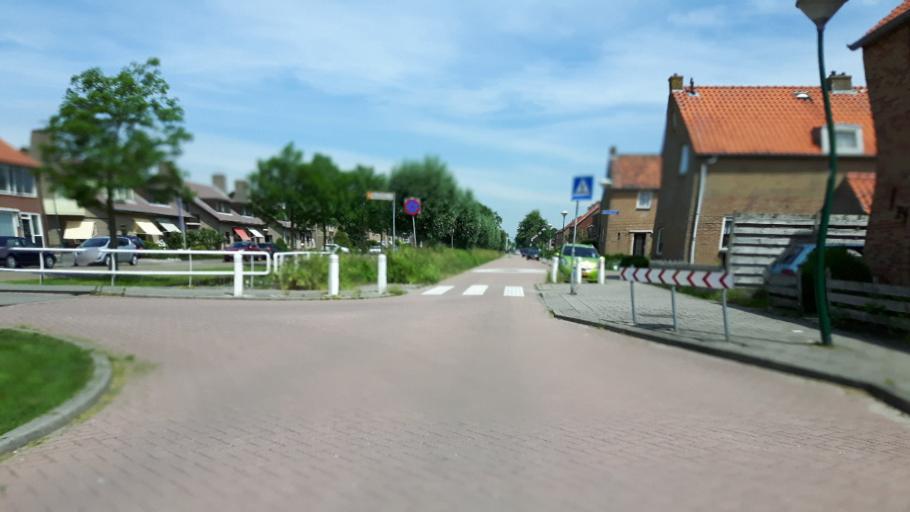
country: NL
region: Utrecht
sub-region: Gemeente Woerden
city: Woerden
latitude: 52.1136
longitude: 4.8346
